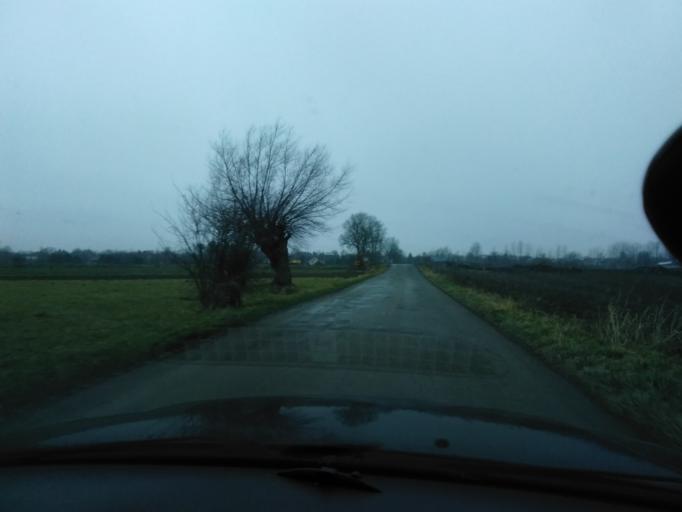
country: PL
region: Subcarpathian Voivodeship
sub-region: Powiat przeworski
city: Zarzecze
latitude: 49.9719
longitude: 22.5610
